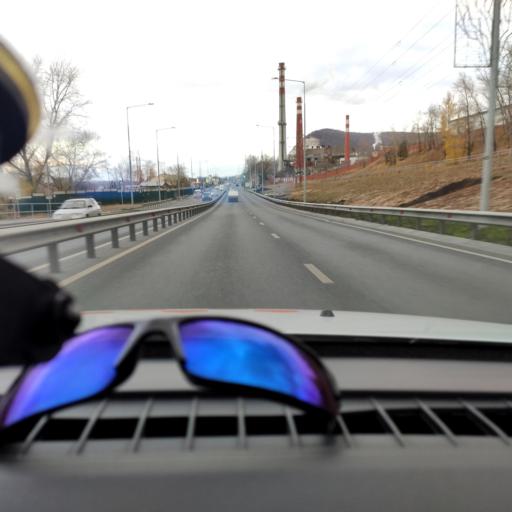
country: RU
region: Samara
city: Volzhskiy
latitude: 53.3758
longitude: 50.1728
